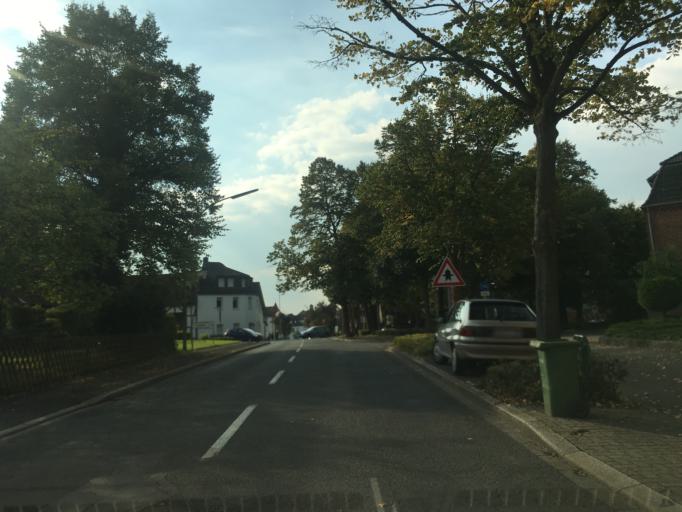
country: DE
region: North Rhine-Westphalia
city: Selm
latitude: 51.7008
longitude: 7.4752
